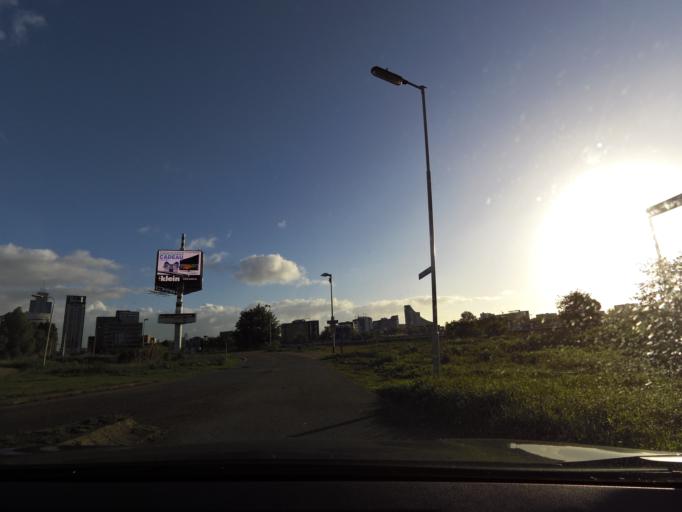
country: NL
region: South Holland
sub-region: Gemeente Rotterdam
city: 's-Gravenland
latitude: 51.9091
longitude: 4.5400
